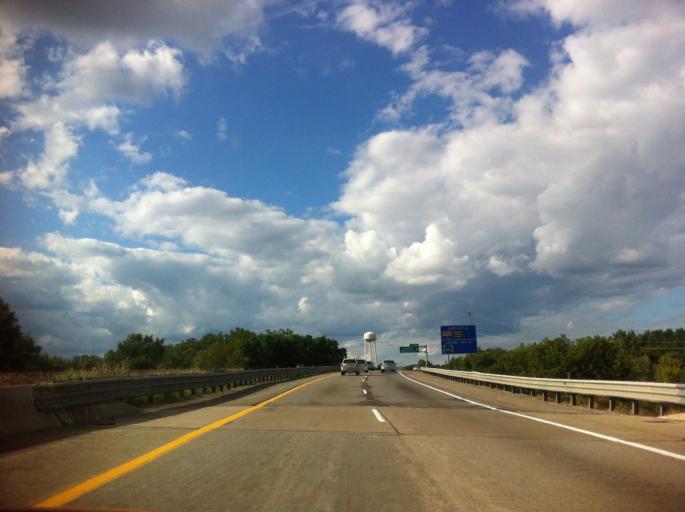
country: US
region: Michigan
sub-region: Livingston County
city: Whitmore Lake
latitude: 42.4224
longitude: -83.7682
